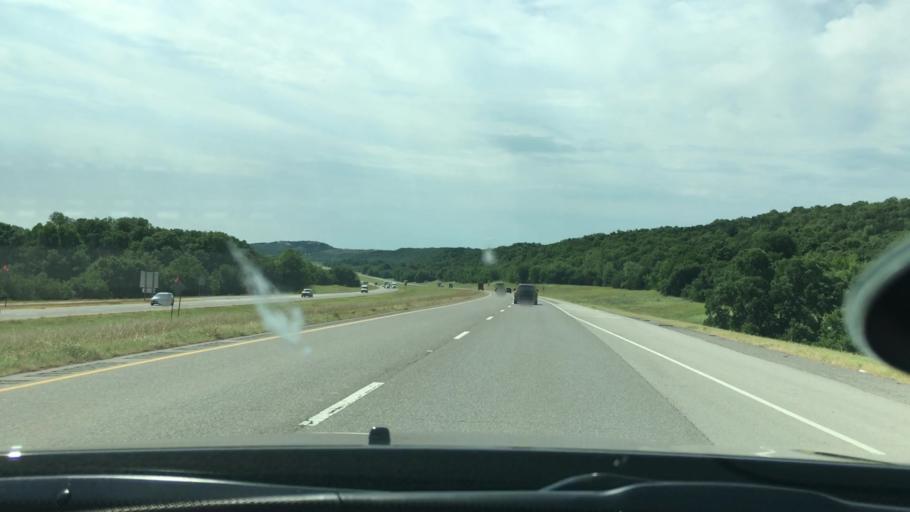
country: US
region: Oklahoma
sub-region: Murray County
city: Davis
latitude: 34.4738
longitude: -97.1558
